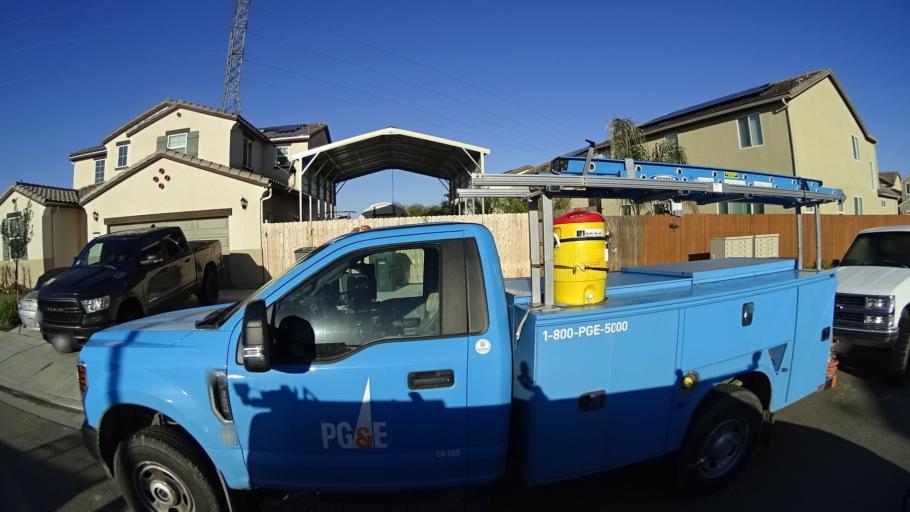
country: US
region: California
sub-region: Fresno County
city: Biola
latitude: 36.8378
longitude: -119.9125
